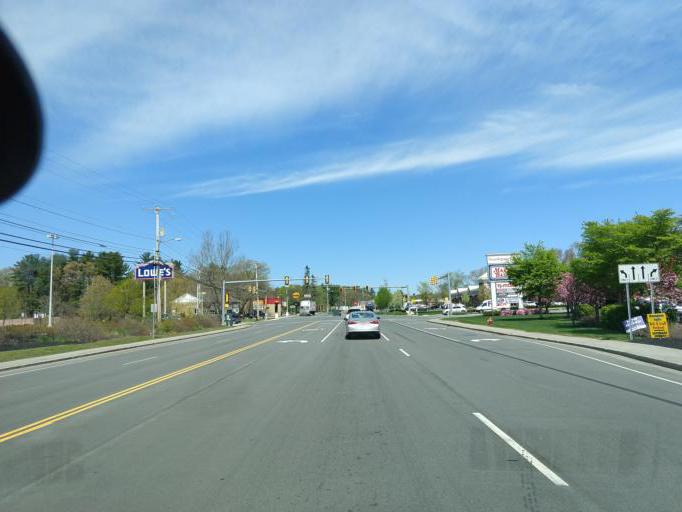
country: US
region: New Hampshire
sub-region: Rockingham County
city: Seabrook
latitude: 42.8860
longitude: -70.8699
